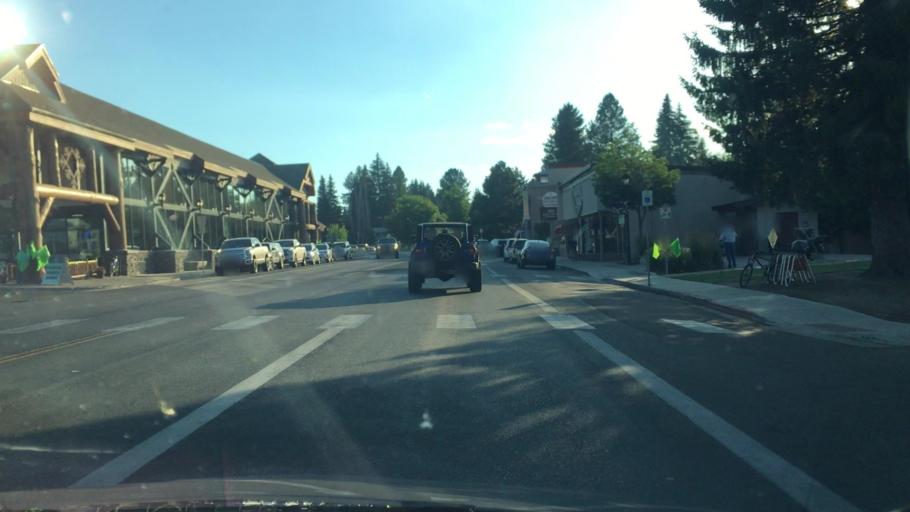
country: US
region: Idaho
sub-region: Valley County
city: McCall
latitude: 44.9110
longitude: -116.0994
